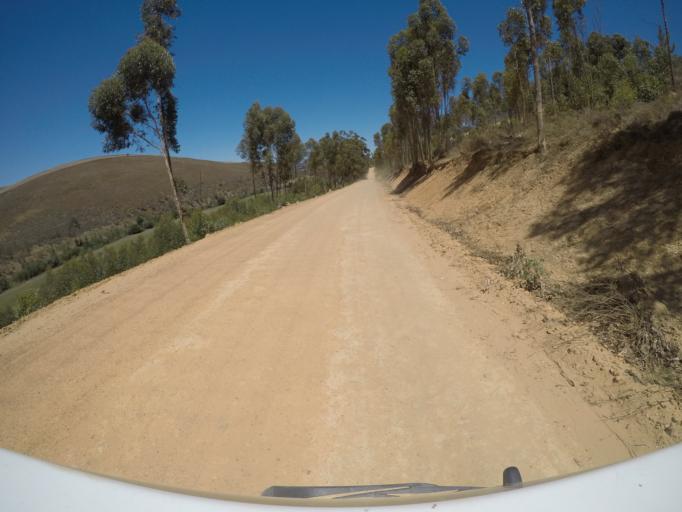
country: ZA
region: Western Cape
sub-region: Overberg District Municipality
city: Grabouw
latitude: -34.2087
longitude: 19.2136
